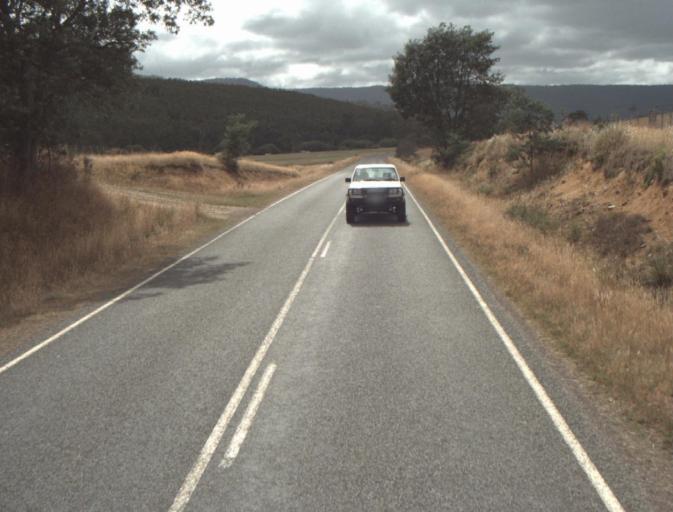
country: AU
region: Tasmania
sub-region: Northern Midlands
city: Evandale
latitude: -41.4708
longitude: 147.5509
